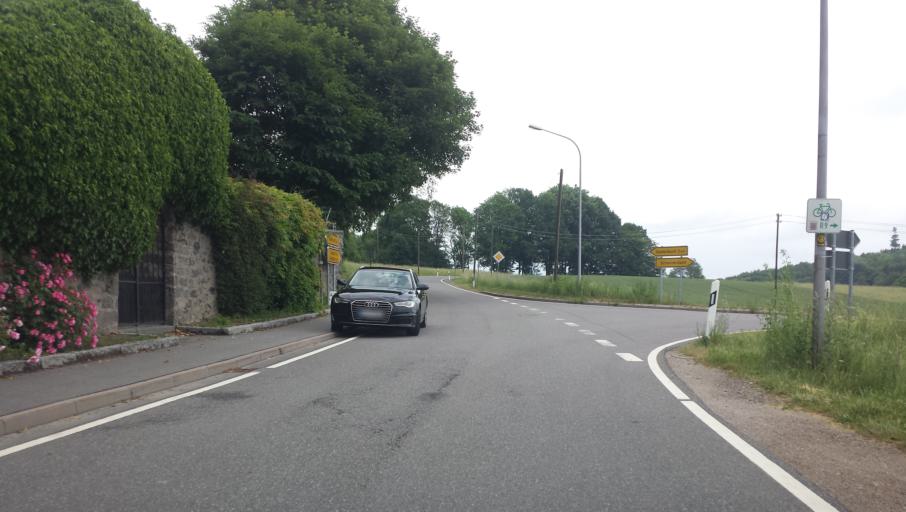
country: DE
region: Hesse
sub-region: Regierungsbezirk Darmstadt
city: Lindenfels
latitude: 49.6932
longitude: 8.7232
